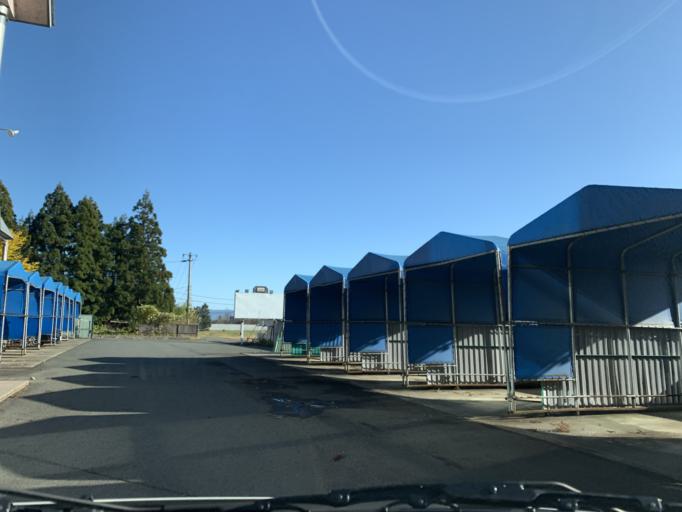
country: JP
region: Iwate
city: Kitakami
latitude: 39.2336
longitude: 141.0769
